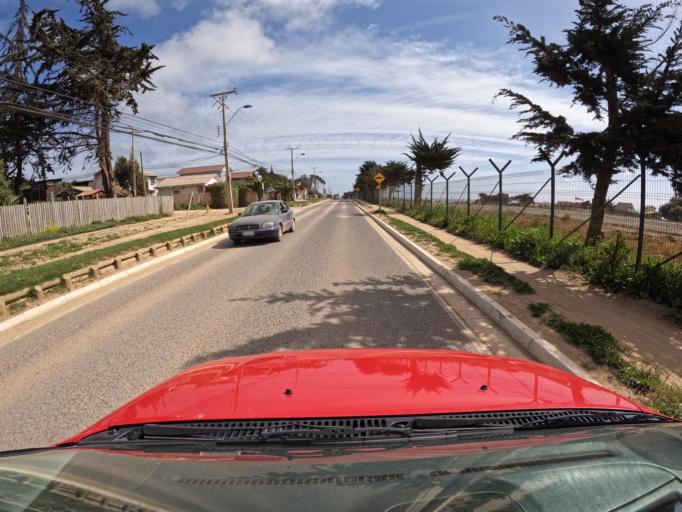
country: CL
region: O'Higgins
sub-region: Provincia de Colchagua
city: Santa Cruz
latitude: -34.3970
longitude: -72.0201
